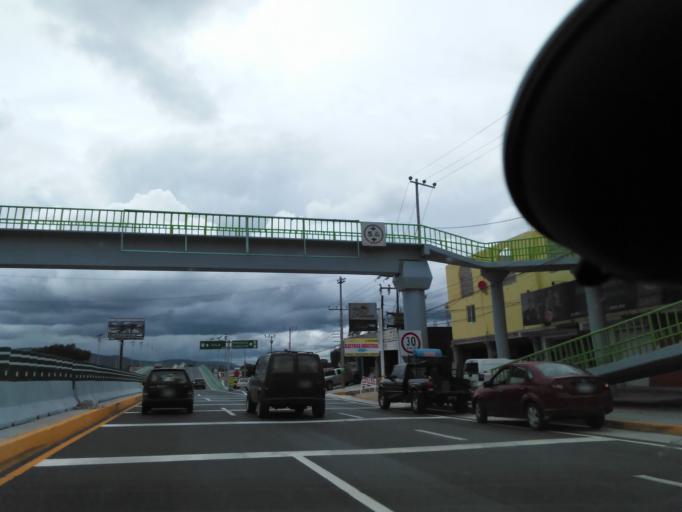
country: MX
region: Hidalgo
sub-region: Tula de Allende
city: Residencial Arboledas
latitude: 20.0544
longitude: -99.3084
